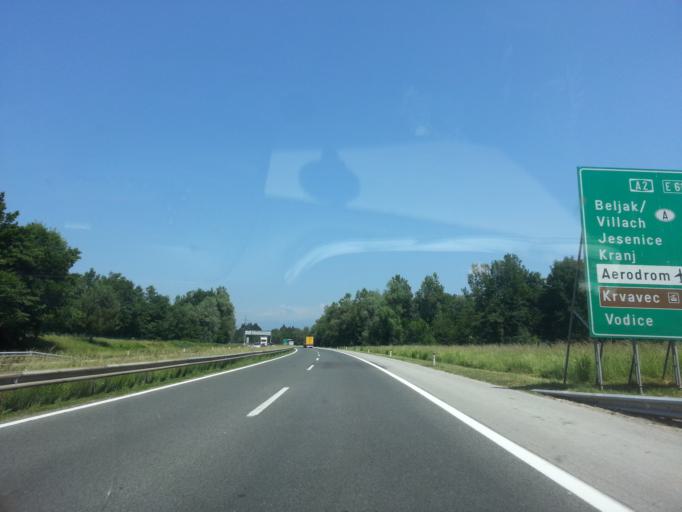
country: SI
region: Medvode
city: Zgornje Pirnice
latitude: 46.1292
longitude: 14.4825
